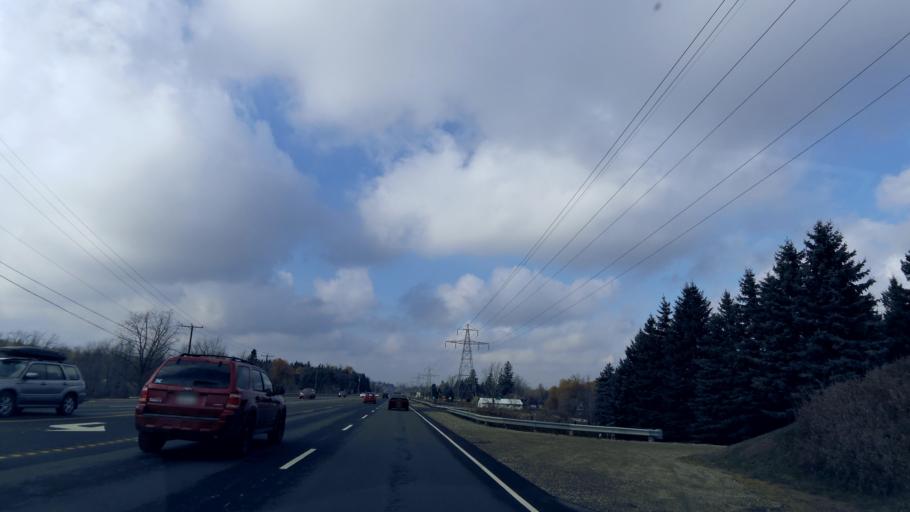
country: CA
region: Ontario
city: Ancaster
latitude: 43.3844
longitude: -80.0159
